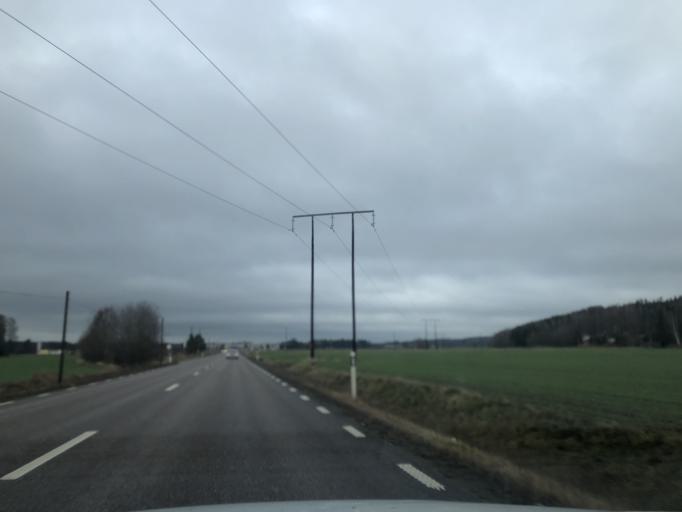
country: SE
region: Vaestra Goetaland
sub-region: Ulricehamns Kommun
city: Ulricehamn
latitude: 57.8377
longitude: 13.4378
